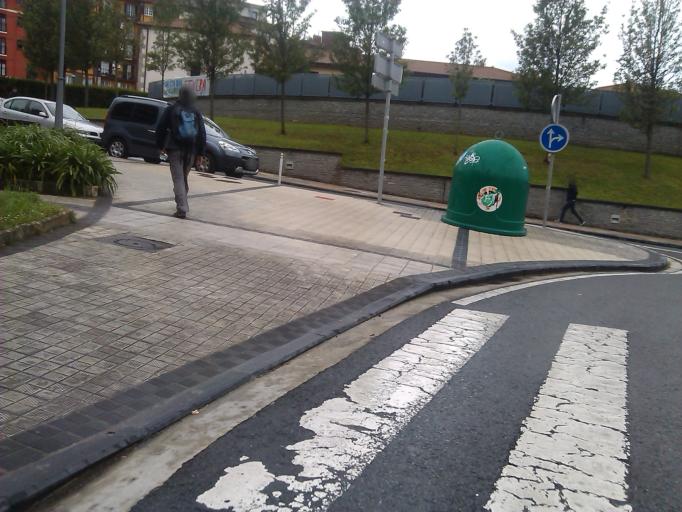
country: ES
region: Basque Country
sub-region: Provincia de Guipuzcoa
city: Hernani
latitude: 43.2685
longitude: -1.9732
